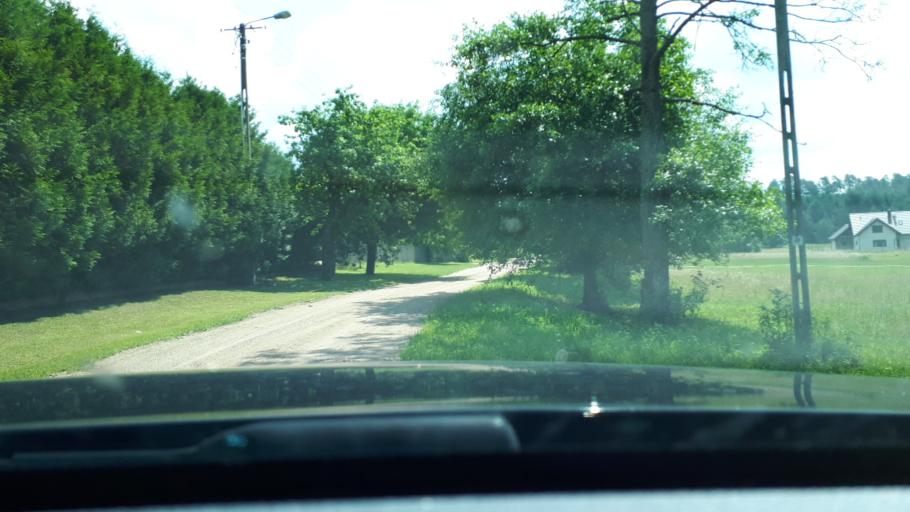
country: PL
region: Podlasie
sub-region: Powiat bialostocki
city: Suprasl
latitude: 53.2445
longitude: 23.3501
